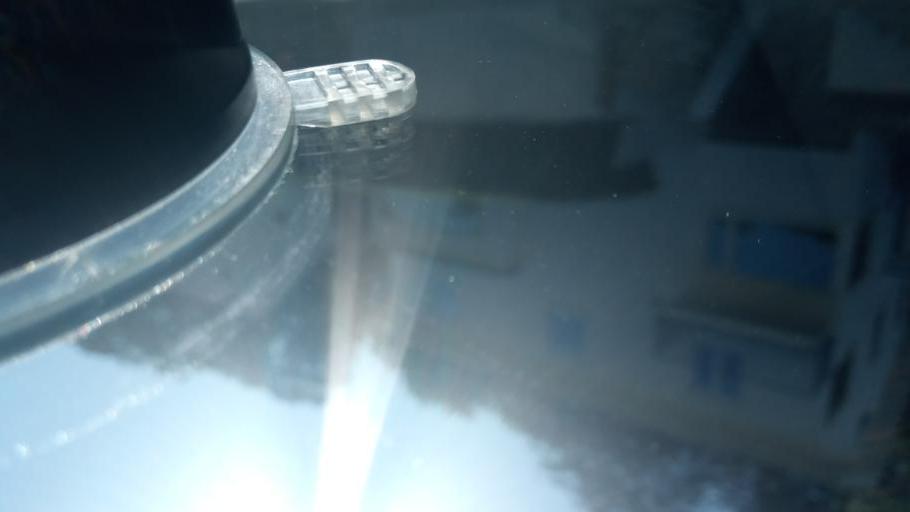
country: SE
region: Vaestra Goetaland
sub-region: Molndal
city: Moelndal
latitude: 57.6920
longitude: 12.0101
